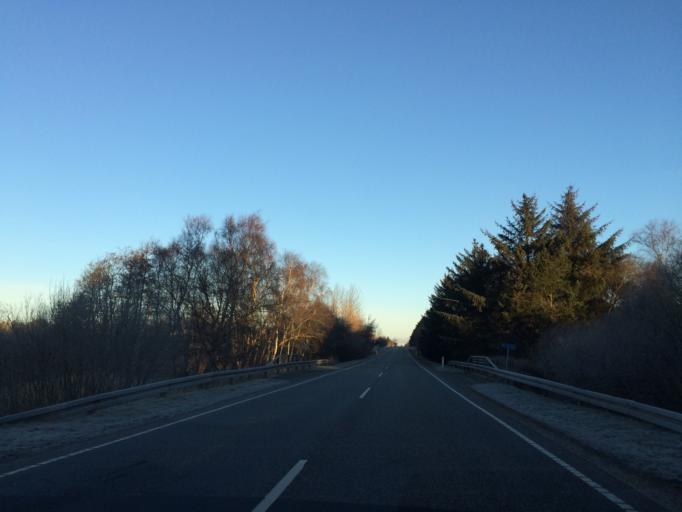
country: DK
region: Central Jutland
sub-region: Holstebro Kommune
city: Ulfborg
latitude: 56.3677
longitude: 8.3343
